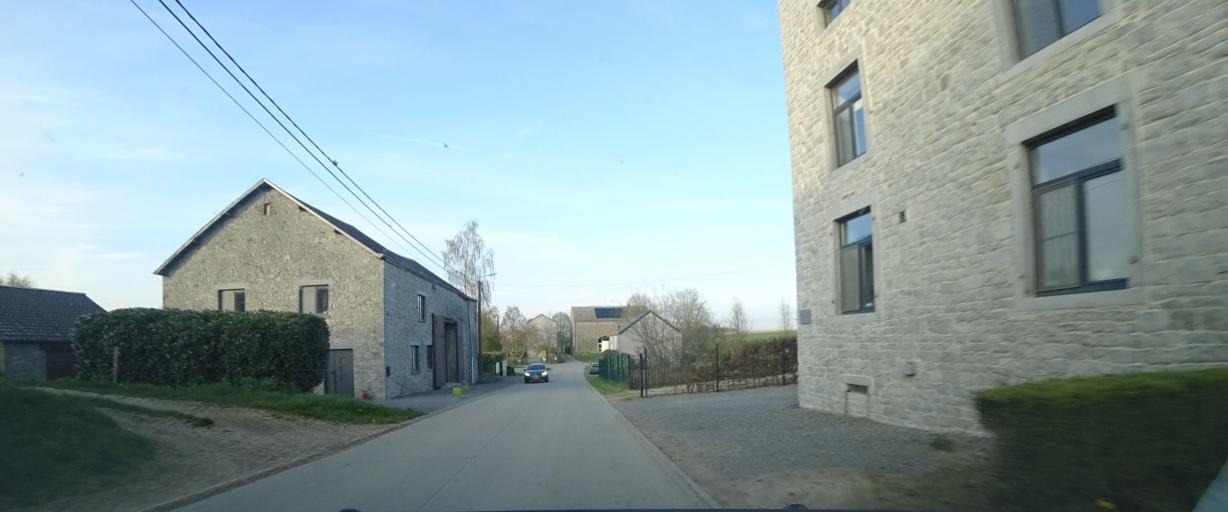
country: BE
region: Wallonia
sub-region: Province de Namur
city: Hamois
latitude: 50.3159
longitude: 5.1515
